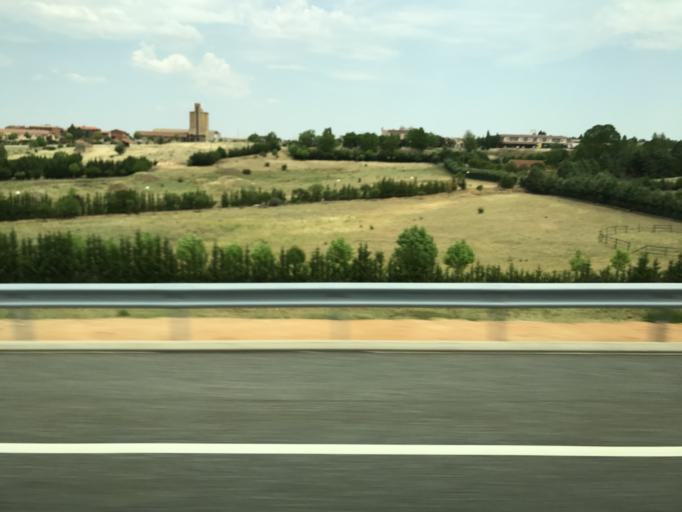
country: ES
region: Castille and Leon
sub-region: Provincia de Segovia
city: Boceguillas
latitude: 41.3308
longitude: -3.6399
